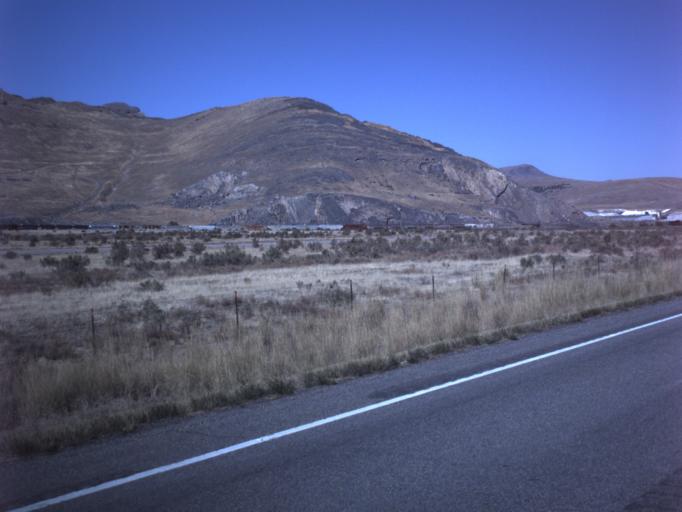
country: US
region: Utah
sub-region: Tooele County
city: Grantsville
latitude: 40.6722
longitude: -112.5480
